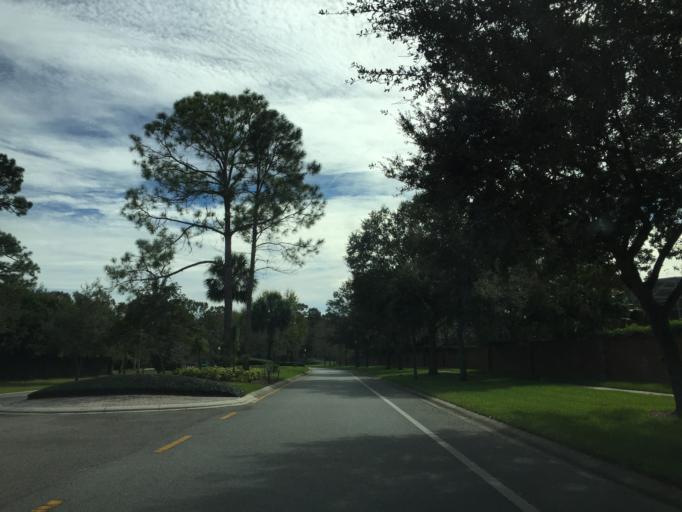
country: US
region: Florida
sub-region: Seminole County
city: Oviedo
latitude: 28.6703
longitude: -81.2349
